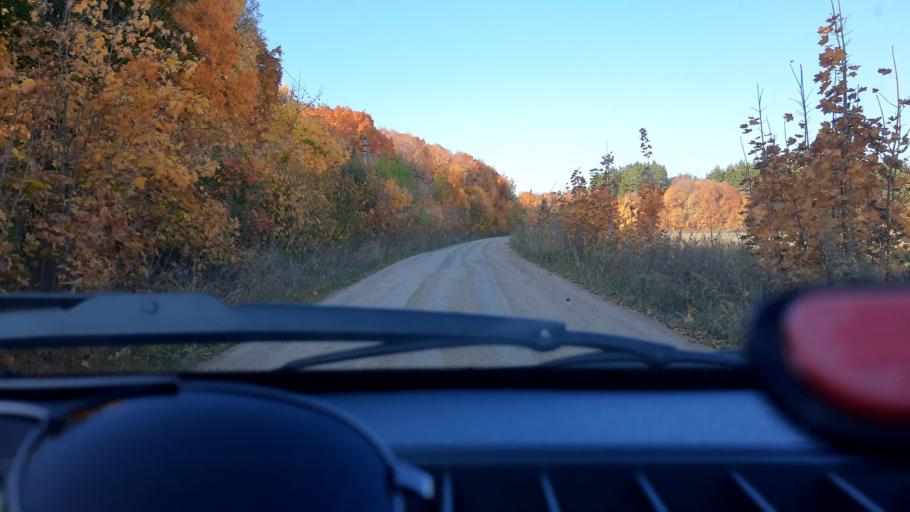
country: RU
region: Bashkortostan
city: Karmaskaly
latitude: 54.3753
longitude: 55.9105
